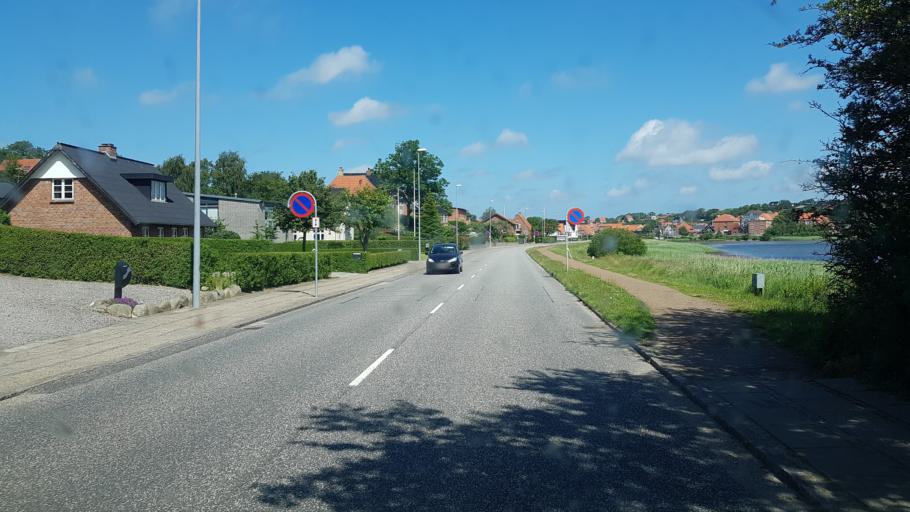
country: DK
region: Central Jutland
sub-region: Lemvig Kommune
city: Lemvig
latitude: 56.5441
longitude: 8.3139
